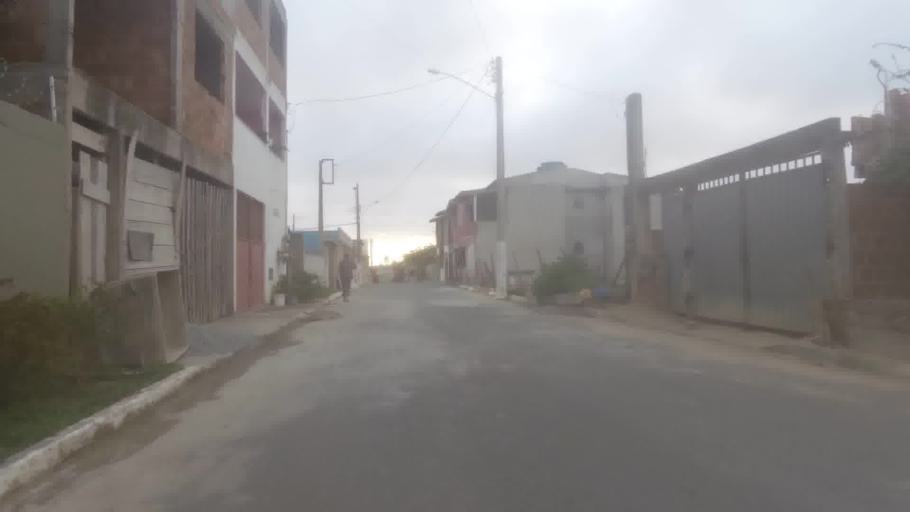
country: BR
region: Espirito Santo
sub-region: Marataizes
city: Marataizes
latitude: -21.0415
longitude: -40.8311
